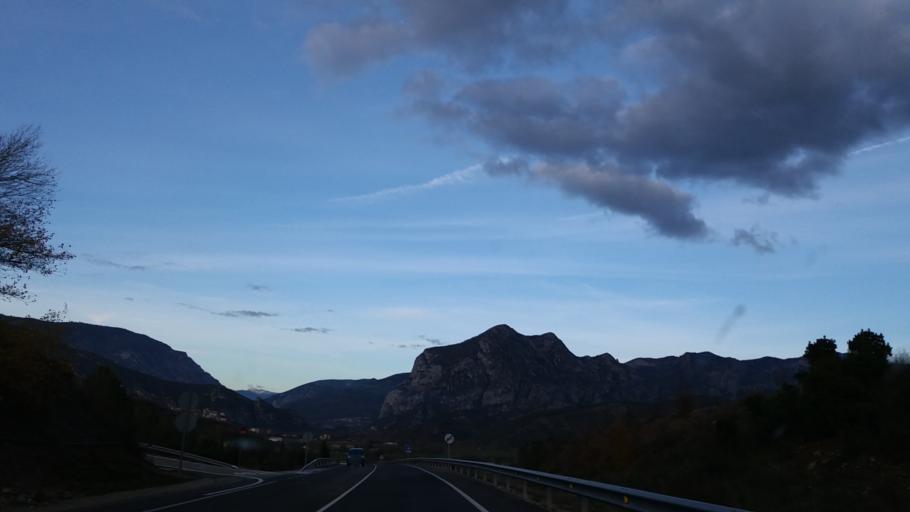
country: ES
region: Catalonia
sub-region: Provincia de Lleida
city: Coll de Nargo
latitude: 42.1561
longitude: 1.3118
